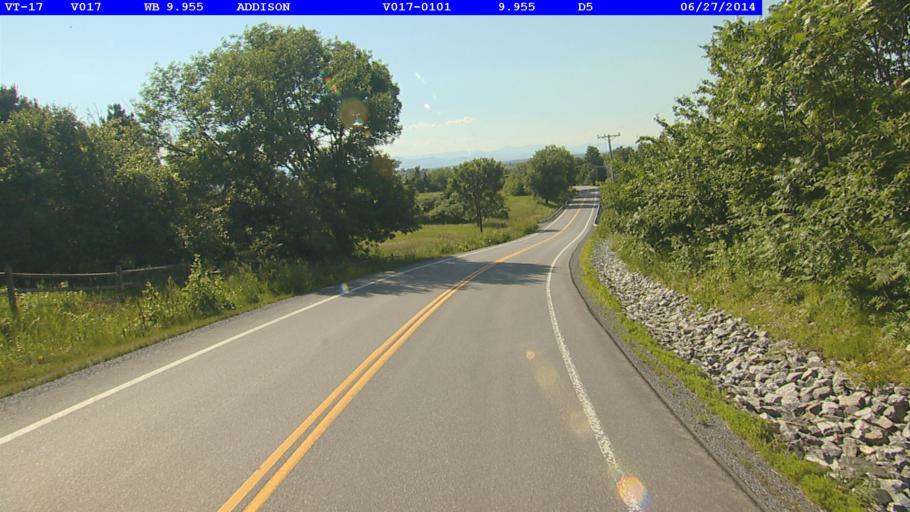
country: US
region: Vermont
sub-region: Addison County
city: Vergennes
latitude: 44.0837
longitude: -73.2731
